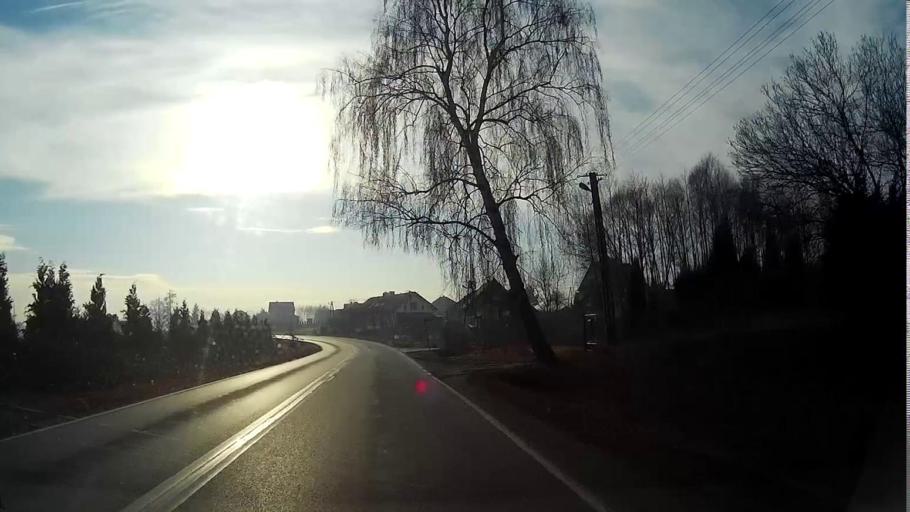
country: PL
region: Lesser Poland Voivodeship
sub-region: Powiat chrzanowski
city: Brodla
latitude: 50.0509
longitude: 19.5672
